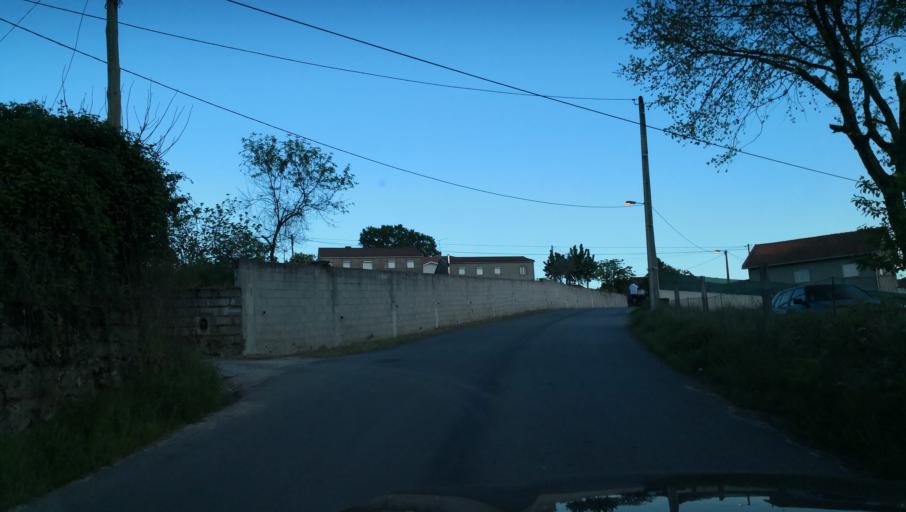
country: PT
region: Vila Real
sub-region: Vila Real
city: Vila Real
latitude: 41.3216
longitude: -7.6770
